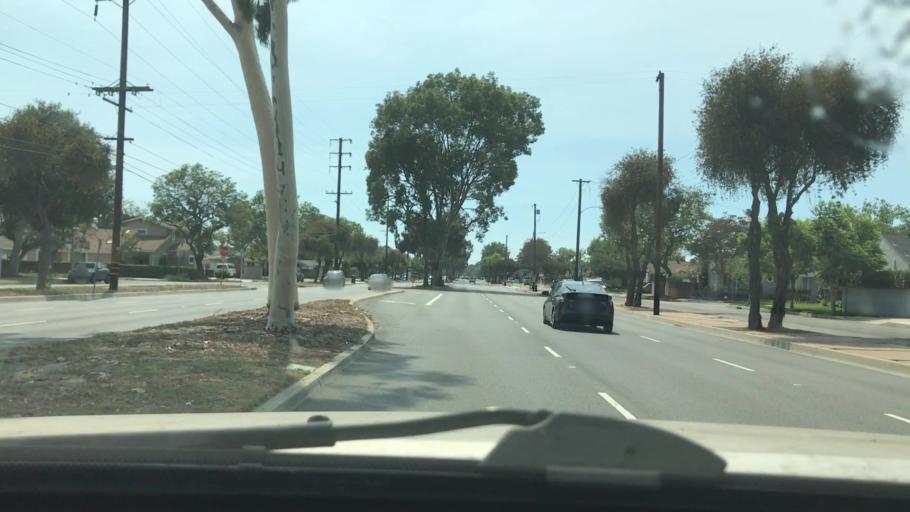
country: US
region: California
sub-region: Orange County
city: Los Alamitos
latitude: 33.8105
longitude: -118.1003
